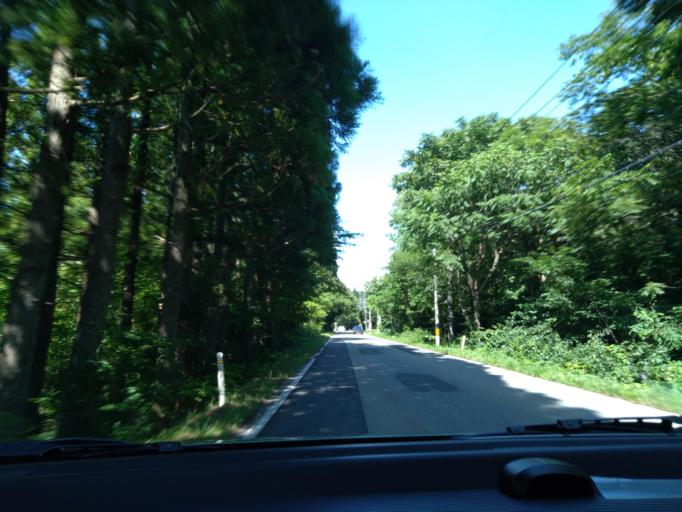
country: JP
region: Akita
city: Kakunodatemachi
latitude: 39.7506
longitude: 140.7245
